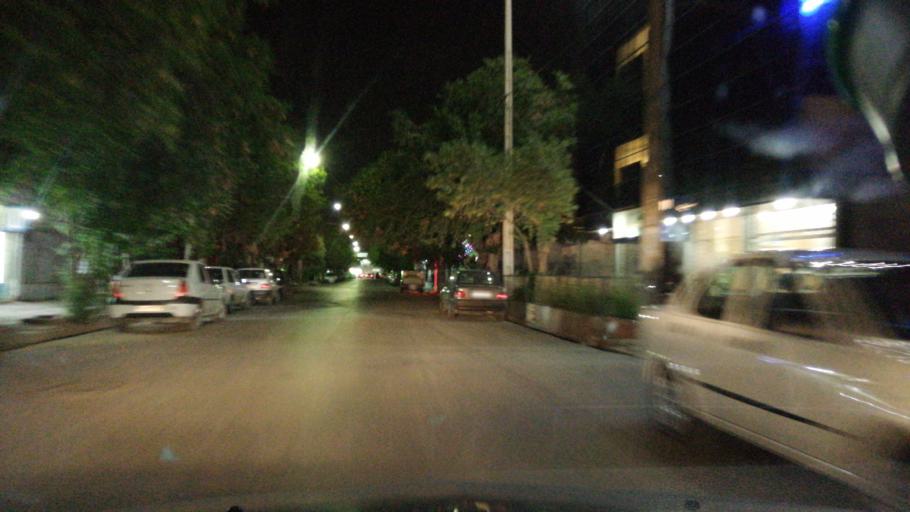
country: IR
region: Razavi Khorasan
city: Mashhad
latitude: 36.3062
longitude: 59.6030
